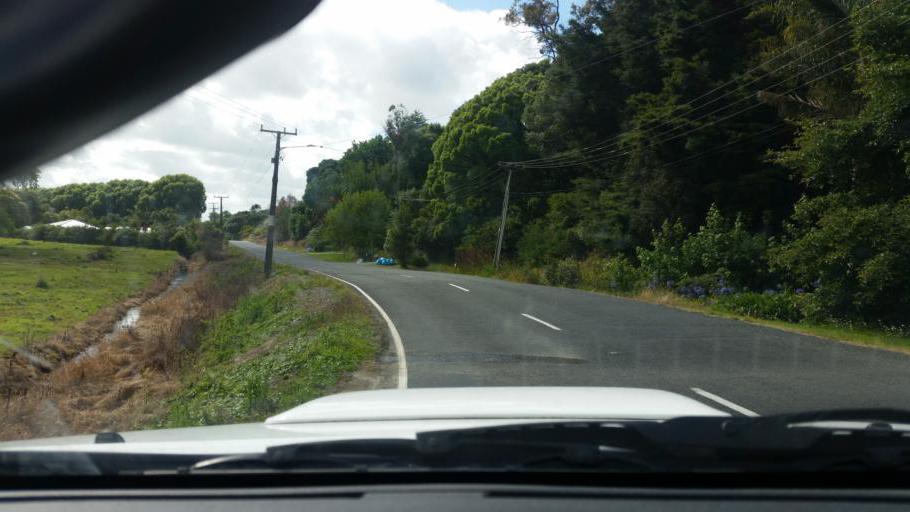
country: NZ
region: Northland
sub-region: Kaipara District
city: Dargaville
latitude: -35.9548
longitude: 173.8598
